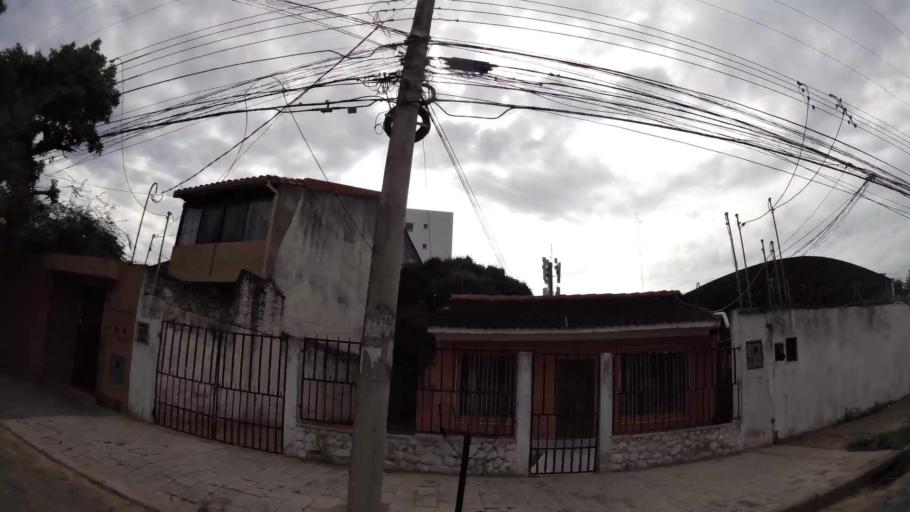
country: BO
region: Santa Cruz
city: Santa Cruz de la Sierra
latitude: -17.7750
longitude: -63.1901
